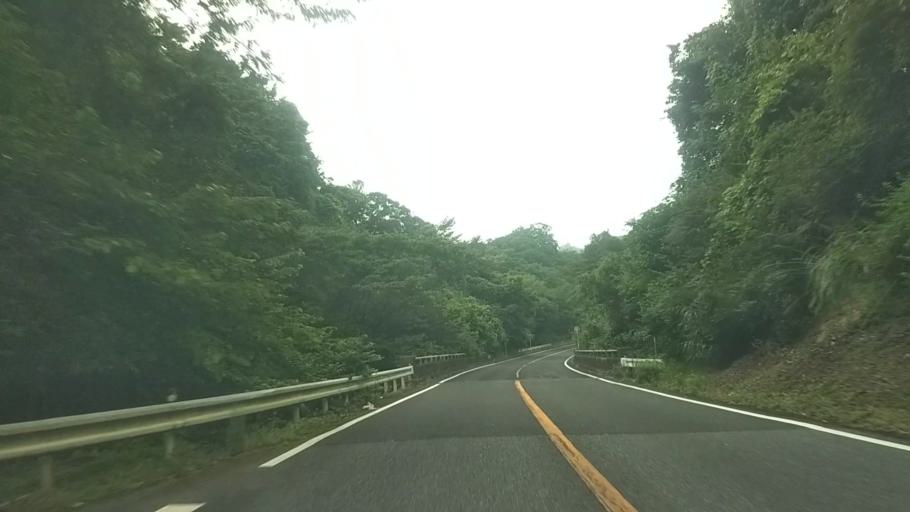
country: JP
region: Chiba
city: Kawaguchi
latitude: 35.2175
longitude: 140.0403
